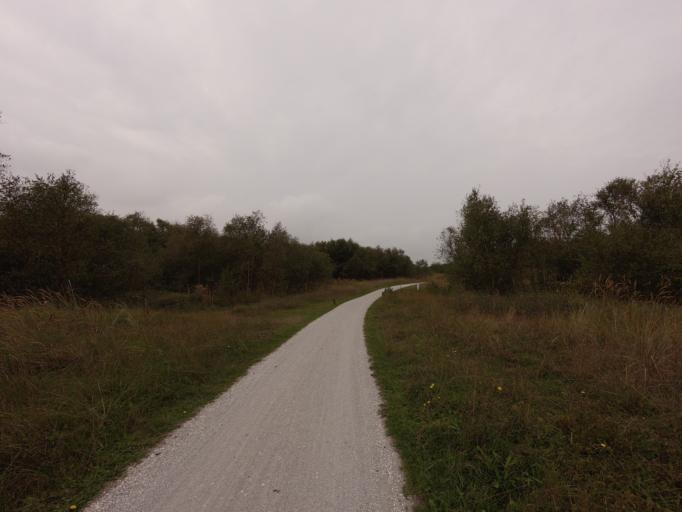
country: NL
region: Friesland
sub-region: Gemeente Schiermonnikoog
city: Schiermonnikoog
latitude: 53.4916
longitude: 6.1984
